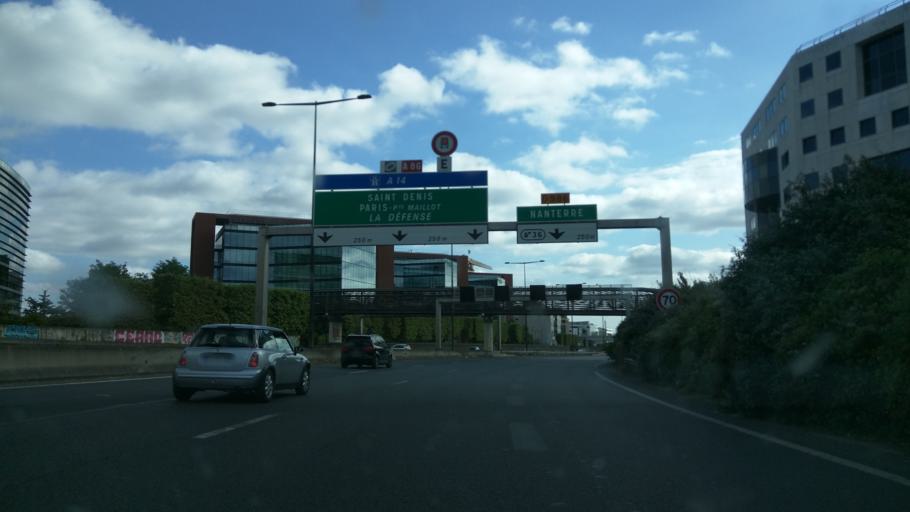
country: FR
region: Ile-de-France
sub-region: Departement des Yvelines
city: Chatou
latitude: 48.8899
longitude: 2.1698
